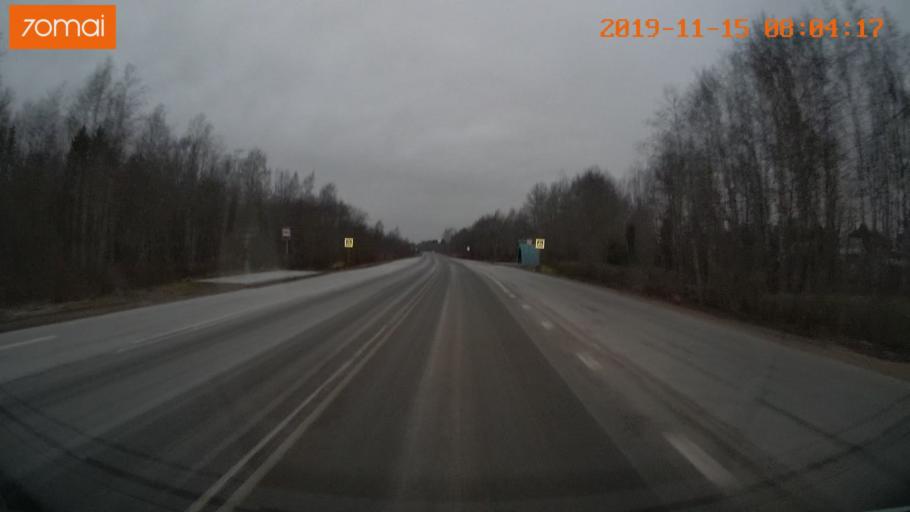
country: RU
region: Vologda
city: Cherepovets
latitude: 59.0060
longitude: 38.0797
